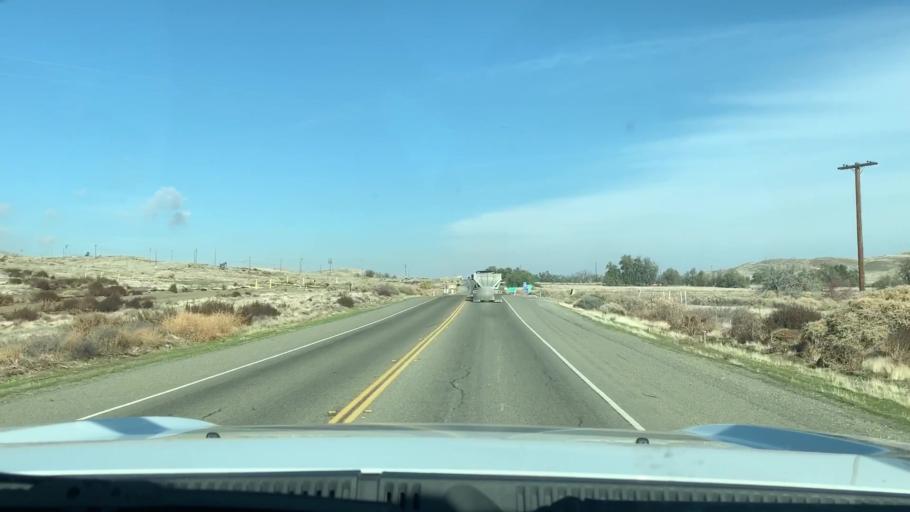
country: US
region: California
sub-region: Fresno County
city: Coalinga
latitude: 36.2434
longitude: -120.3150
